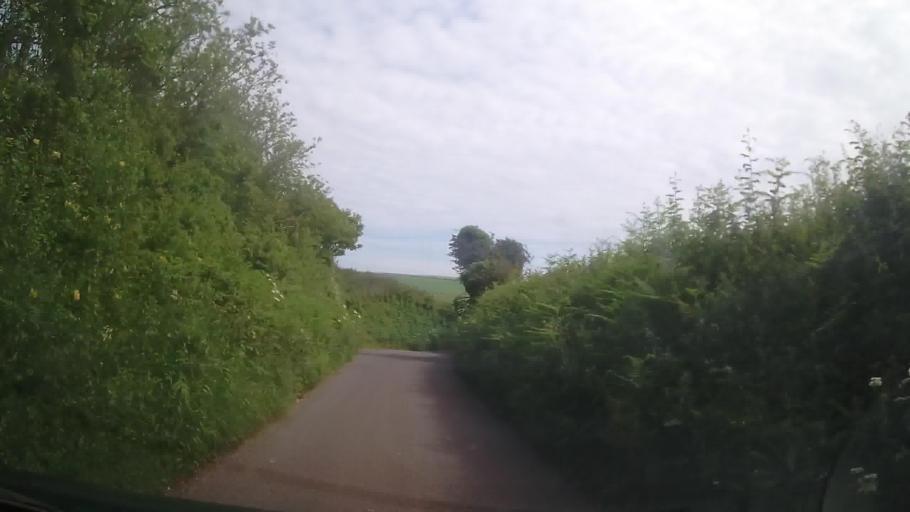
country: GB
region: England
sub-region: Devon
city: Salcombe
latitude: 50.2430
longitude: -3.6800
